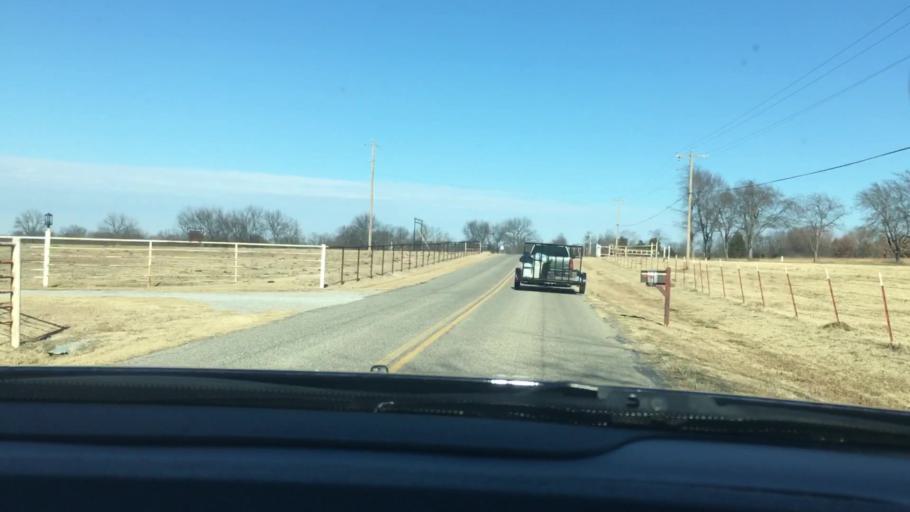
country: US
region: Oklahoma
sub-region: Murray County
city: Davis
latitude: 34.4815
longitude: -97.0556
